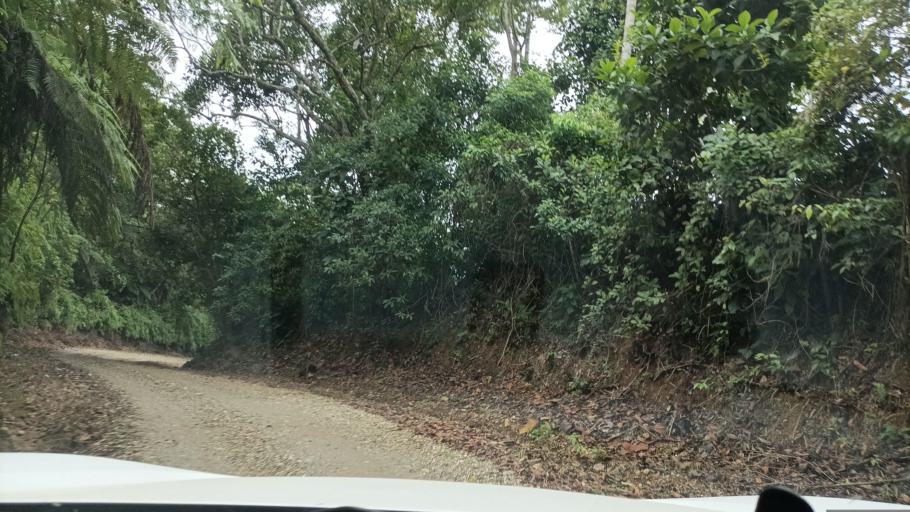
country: MX
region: Veracruz
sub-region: Uxpanapa
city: Poblado 10
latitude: 17.4424
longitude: -94.4082
